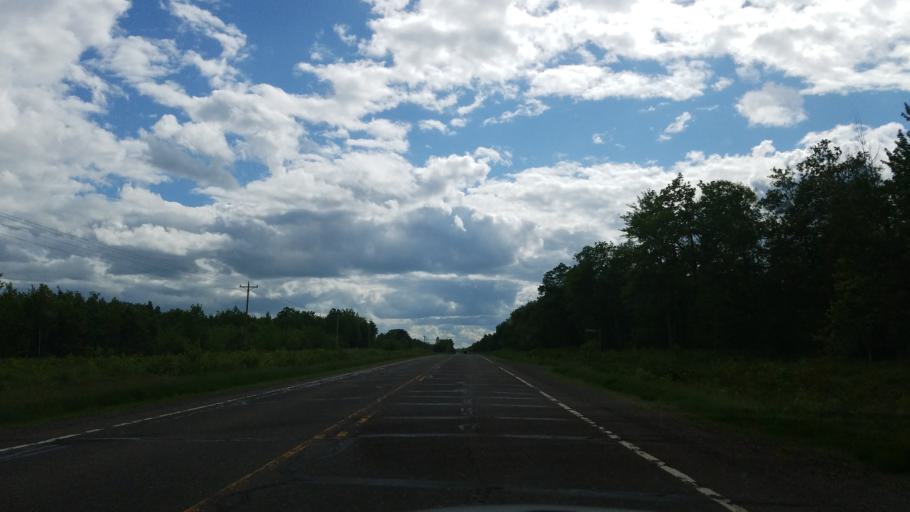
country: US
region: Wisconsin
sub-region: Washburn County
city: Spooner
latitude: 46.1992
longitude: -92.1597
